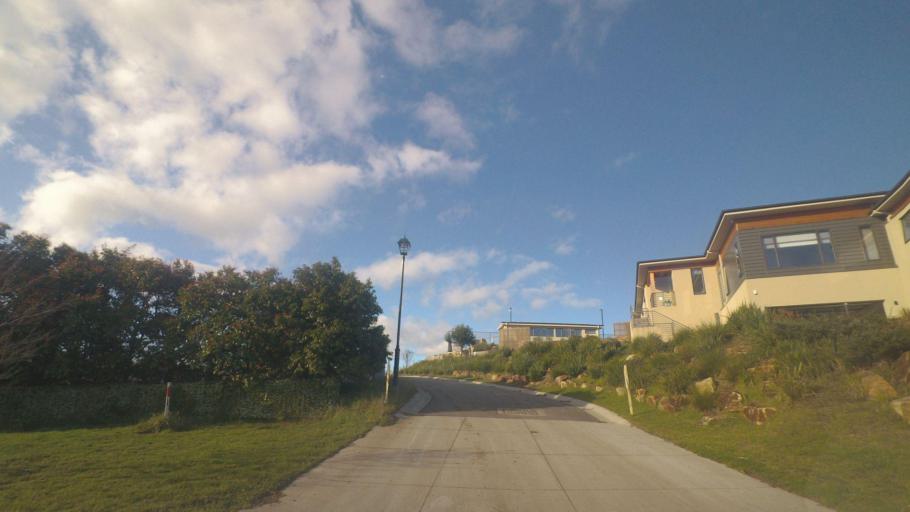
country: AU
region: Victoria
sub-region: Yarra Ranges
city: Lysterfield
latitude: -37.9163
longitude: 145.2932
